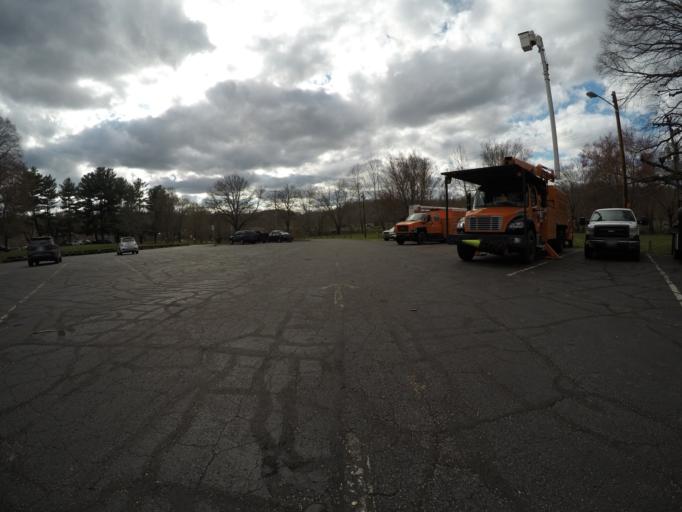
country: US
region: Ohio
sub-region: Washington County
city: Marietta
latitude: 39.4327
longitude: -81.4700
